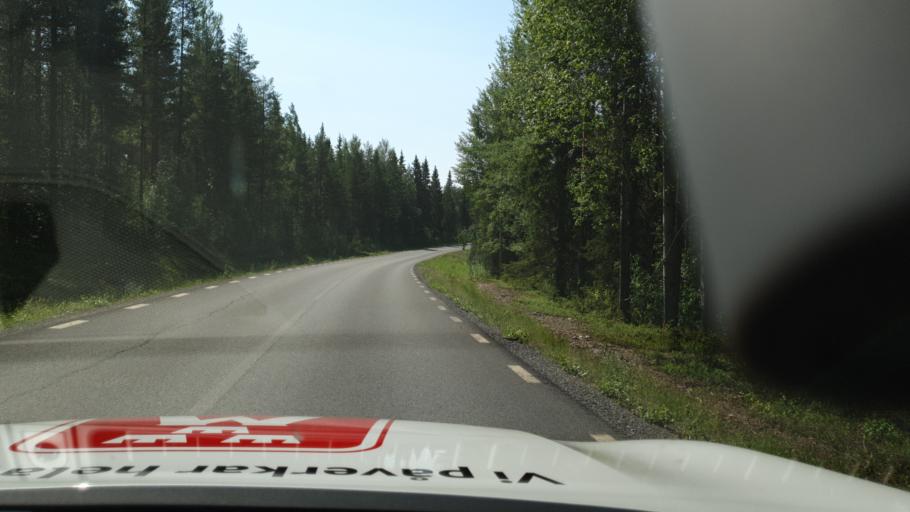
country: SE
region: Vaesterbotten
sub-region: Skelleftea Kommun
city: Langsele
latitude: 64.9641
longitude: 20.0439
